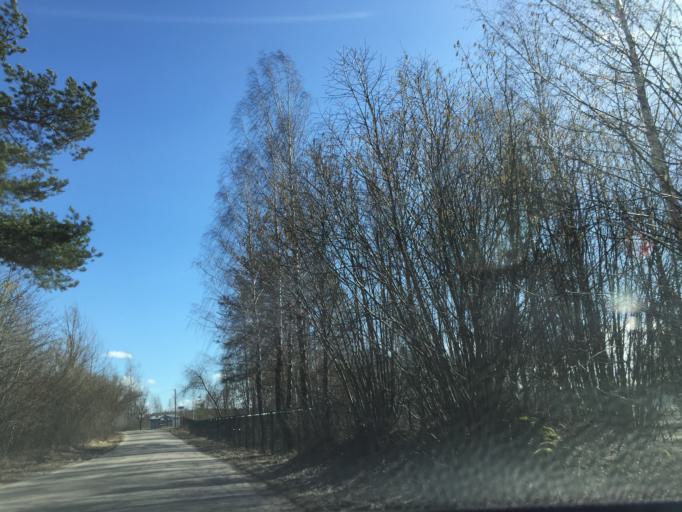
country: LV
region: Salaspils
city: Salaspils
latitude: 56.8438
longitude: 24.4243
